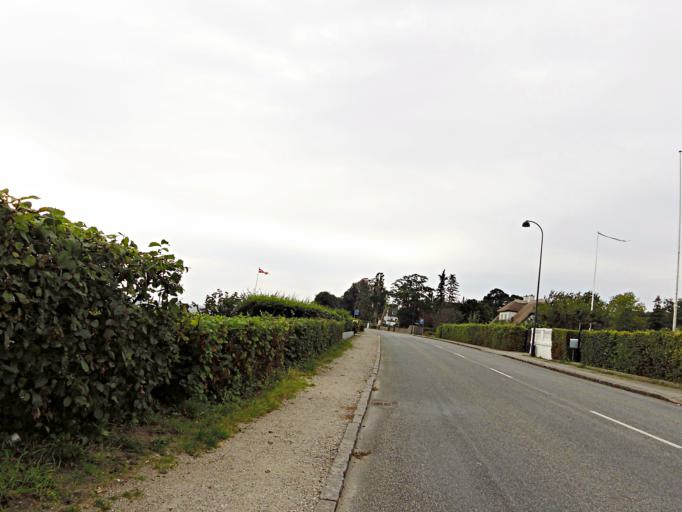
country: DK
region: Capital Region
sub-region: Rudersdal Kommune
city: Trorod
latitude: 55.8108
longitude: 12.5775
